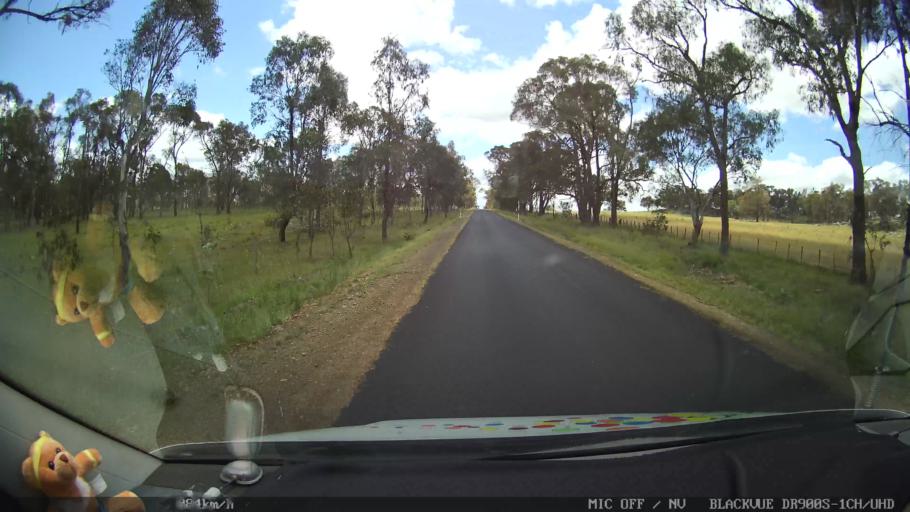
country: AU
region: New South Wales
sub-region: Glen Innes Severn
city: Glen Innes
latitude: -29.4229
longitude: 151.7093
